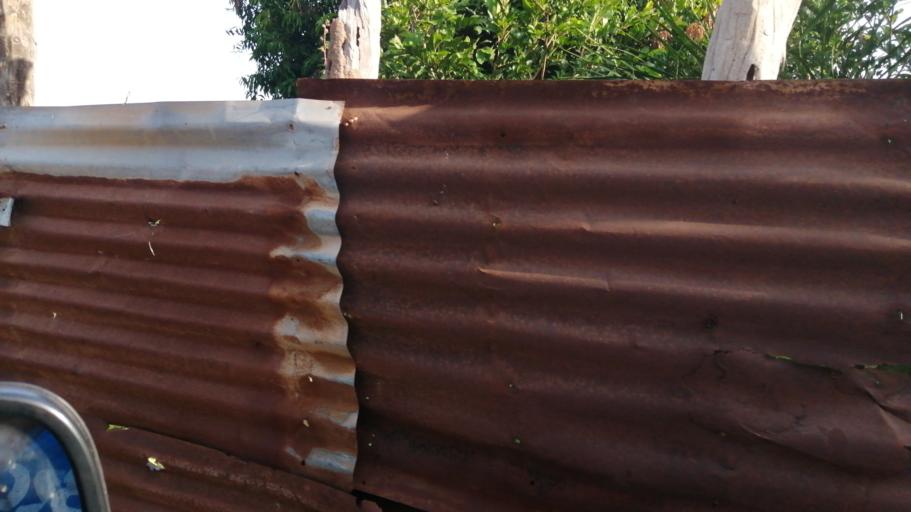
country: GW
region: Oio
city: Mansoa
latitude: 11.9996
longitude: -15.4697
